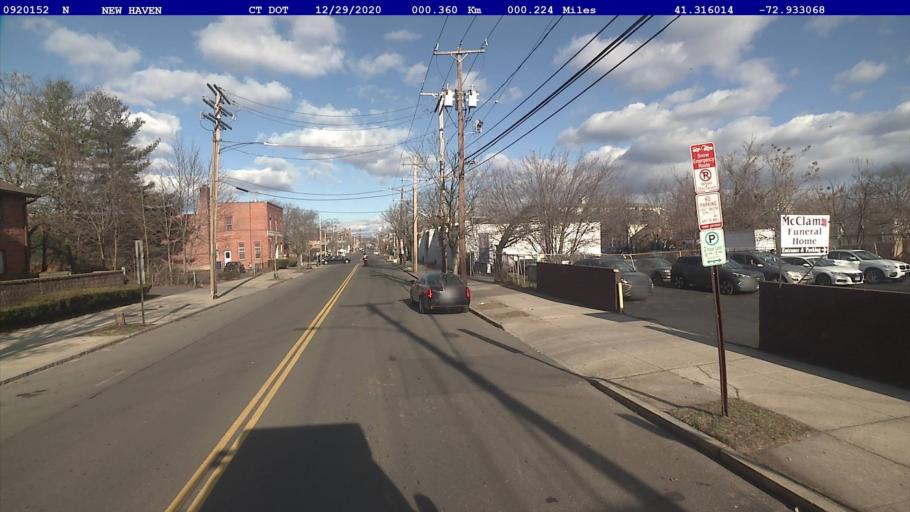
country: US
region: Connecticut
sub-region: New Haven County
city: New Haven
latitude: 41.3160
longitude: -72.9331
